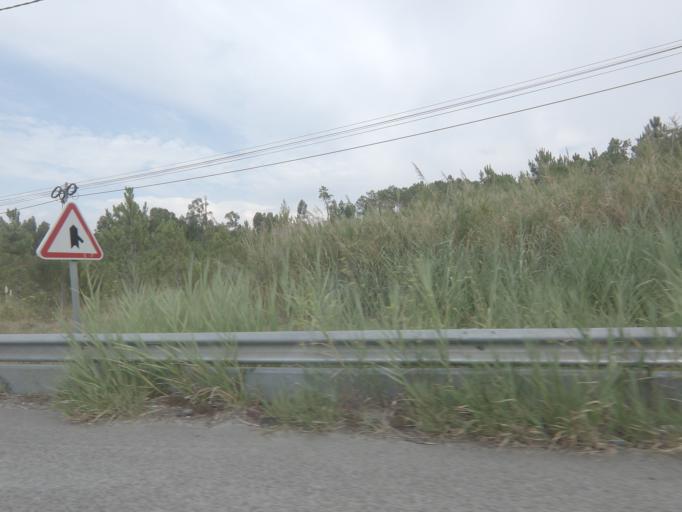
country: PT
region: Coimbra
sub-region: Condeixa-A-Nova
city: Condeixa-a-Nova
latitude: 40.1444
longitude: -8.4650
